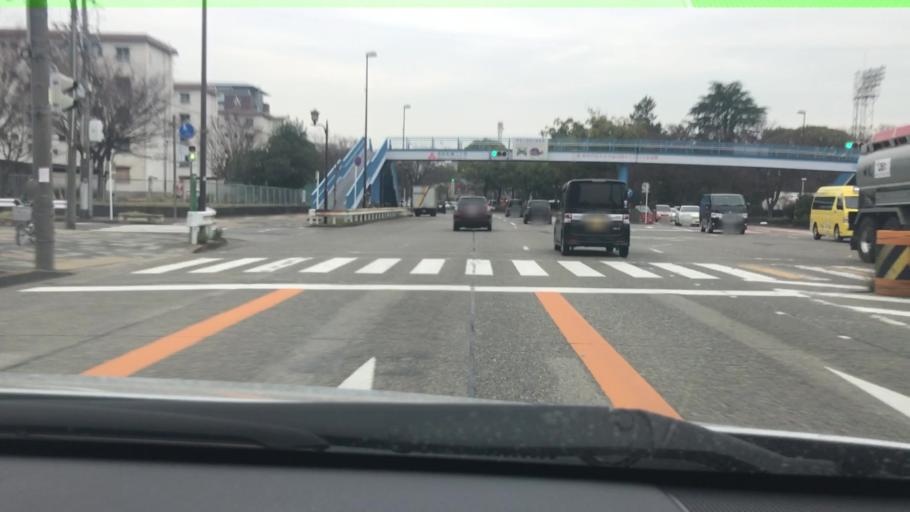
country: JP
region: Aichi
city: Nagoya-shi
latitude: 35.1914
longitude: 136.9037
